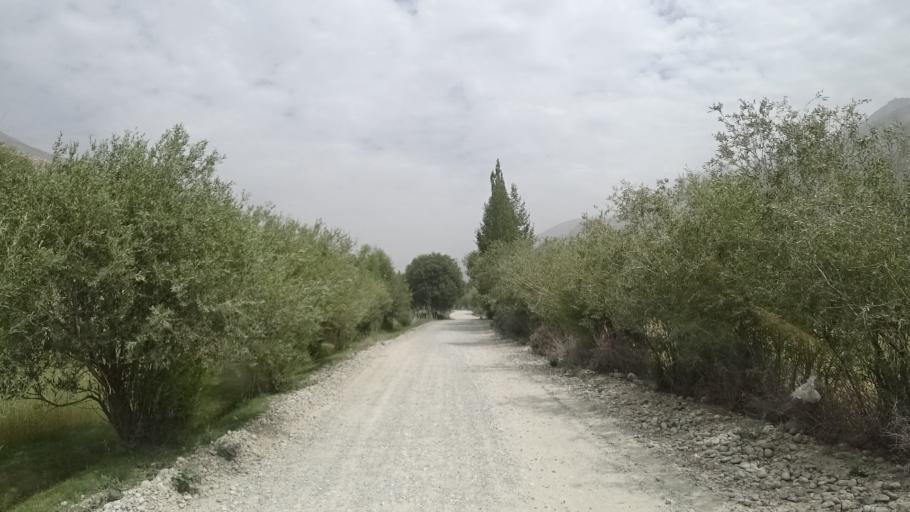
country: AF
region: Badakhshan
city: Khandud
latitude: 37.0427
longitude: 72.6645
